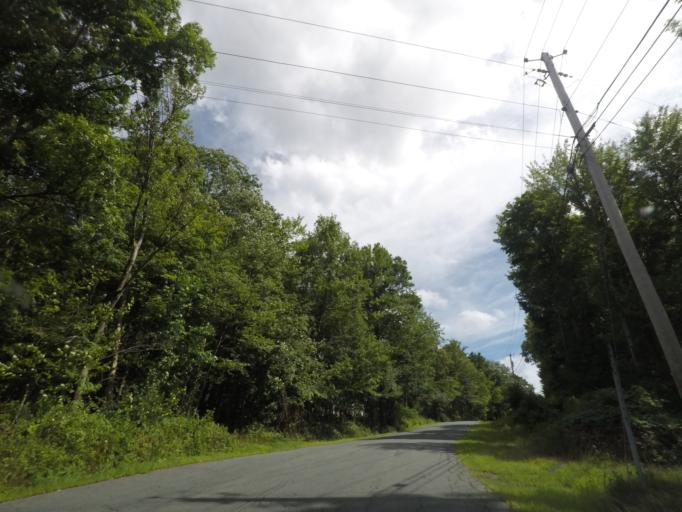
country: US
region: New York
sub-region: Rensselaer County
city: Poestenkill
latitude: 42.6853
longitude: -73.5518
